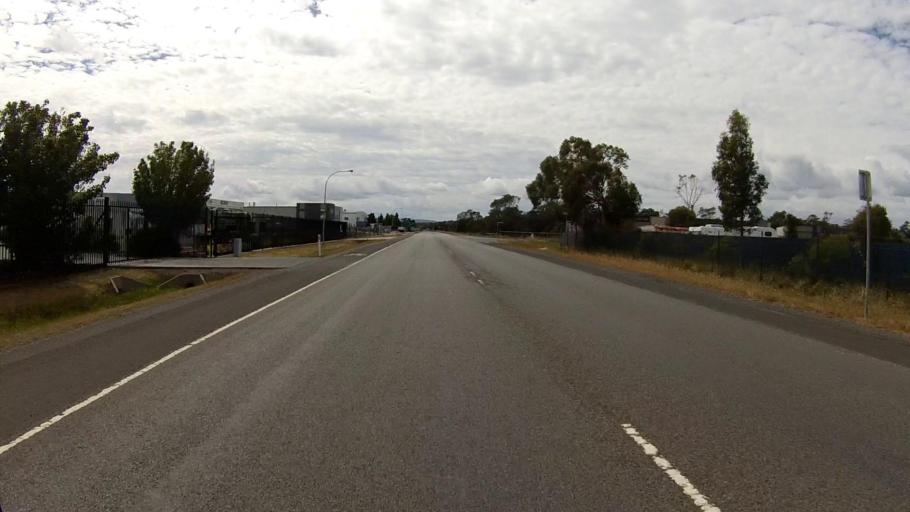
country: AU
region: Tasmania
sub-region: Clarence
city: Cambridge
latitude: -42.8310
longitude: 147.4812
